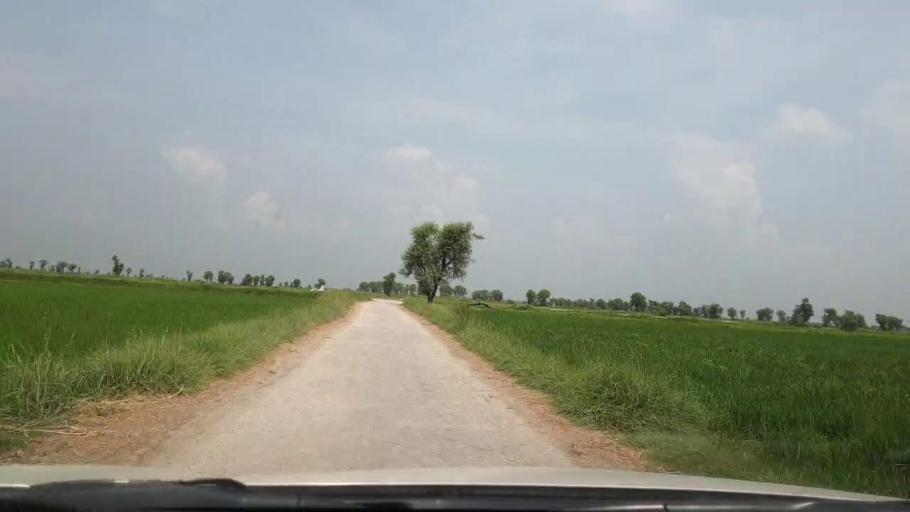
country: PK
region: Sindh
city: Dokri
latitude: 27.3917
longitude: 68.0545
